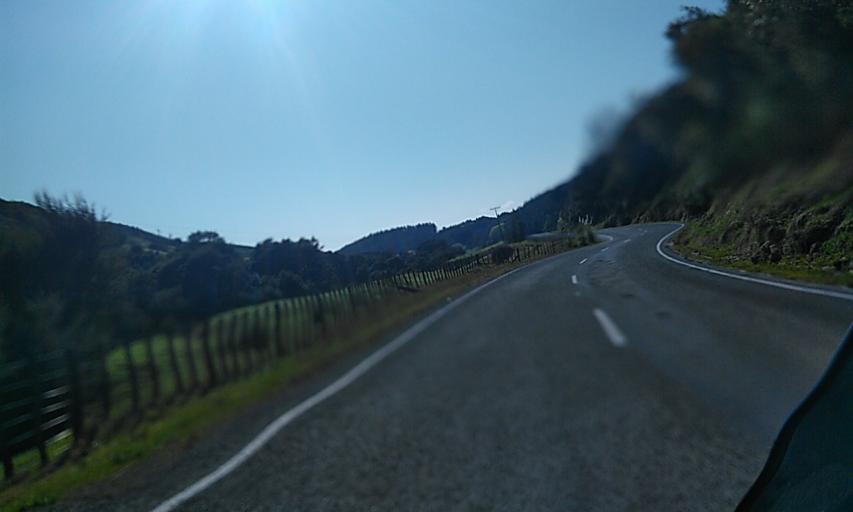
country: NZ
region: Gisborne
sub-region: Gisborne District
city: Gisborne
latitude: -38.5846
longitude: 178.0026
